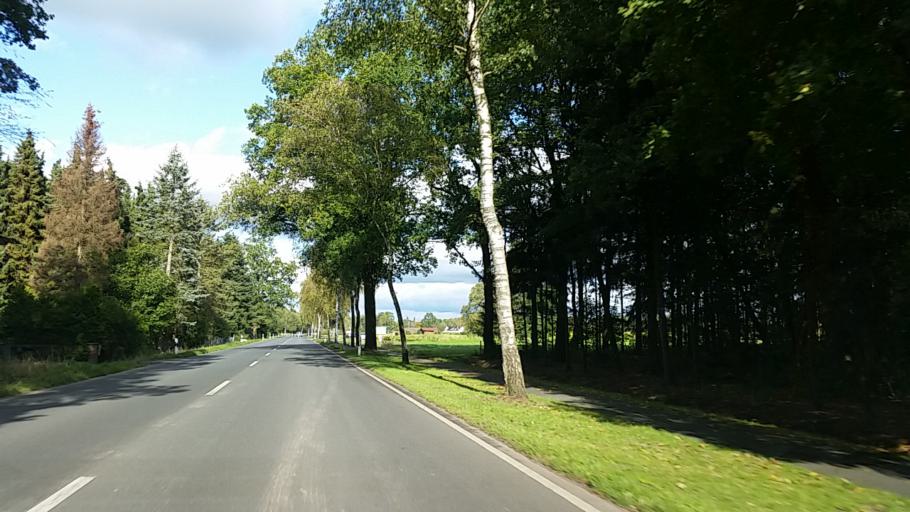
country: DE
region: Lower Saxony
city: Welle
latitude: 53.1783
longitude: 9.8177
